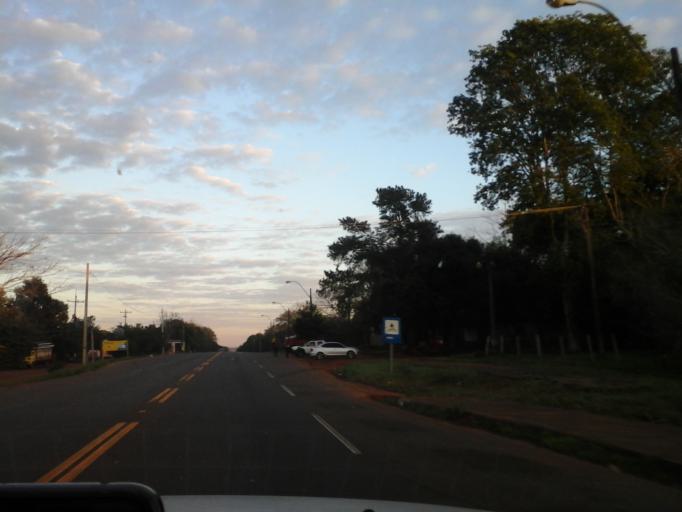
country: PY
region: Misiones
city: Santiago
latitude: -27.0452
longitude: -56.6520
